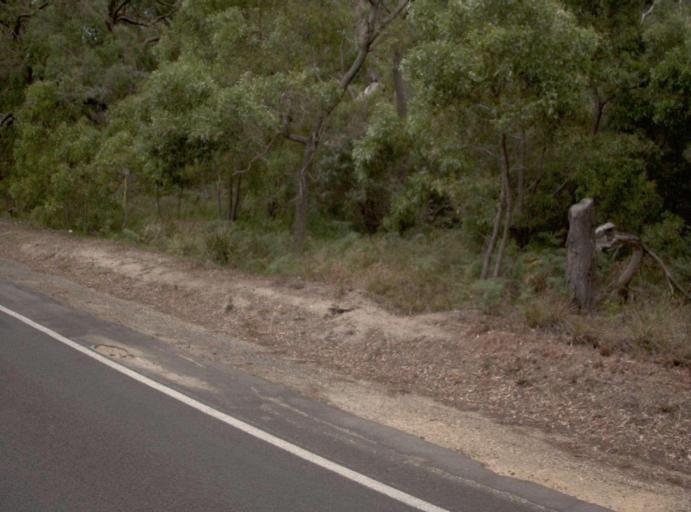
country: AU
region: Victoria
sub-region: Wellington
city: Sale
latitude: -38.2136
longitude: 147.0630
